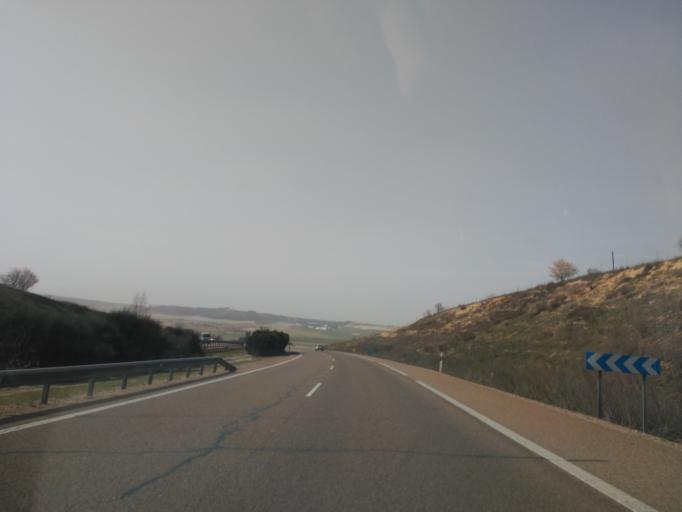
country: ES
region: Castille and Leon
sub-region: Provincia de Valladolid
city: Fuensaldana
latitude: 41.6768
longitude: -4.7532
